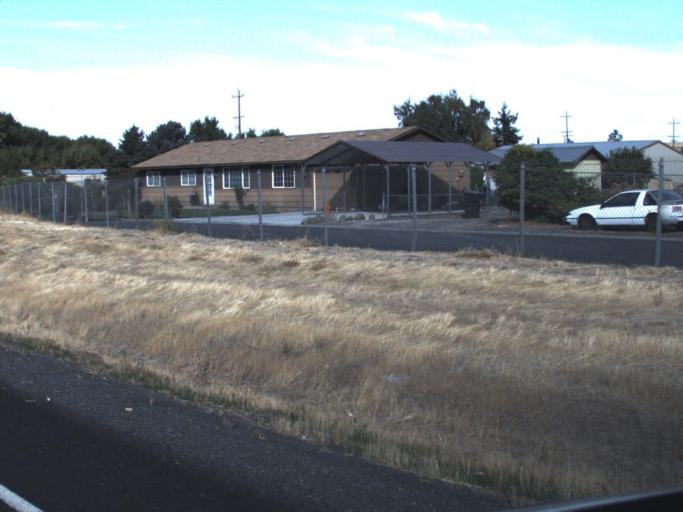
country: US
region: Washington
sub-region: Franklin County
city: Connell
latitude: 46.6524
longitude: -118.8669
